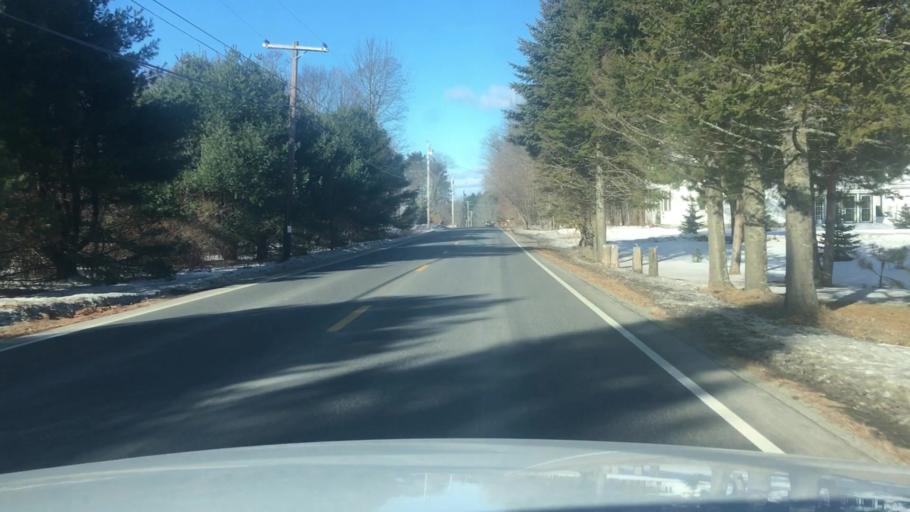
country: US
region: Maine
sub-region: Somerset County
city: Skowhegan
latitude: 44.7420
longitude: -69.6896
